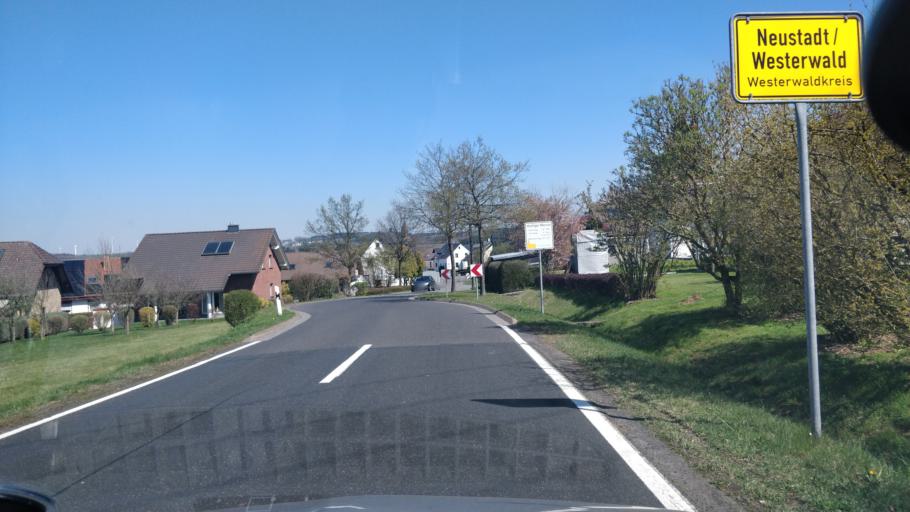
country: DE
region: Rheinland-Pfalz
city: Niederrossbach
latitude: 50.6280
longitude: 8.0389
